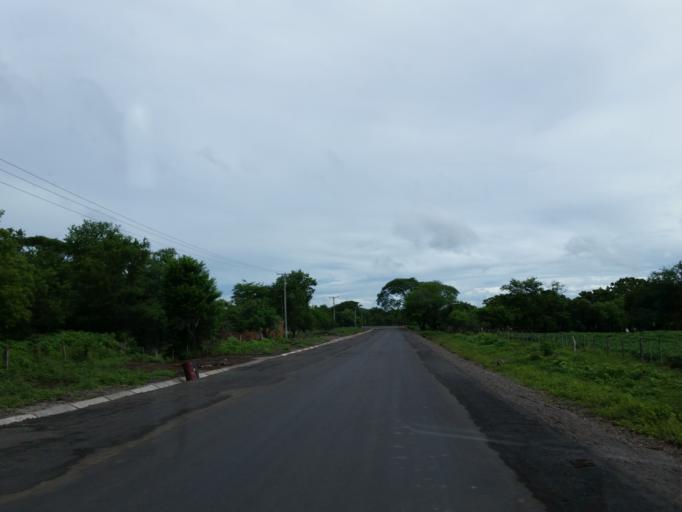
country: NI
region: Leon
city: Larreynaga
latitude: 12.5217
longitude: -86.6016
